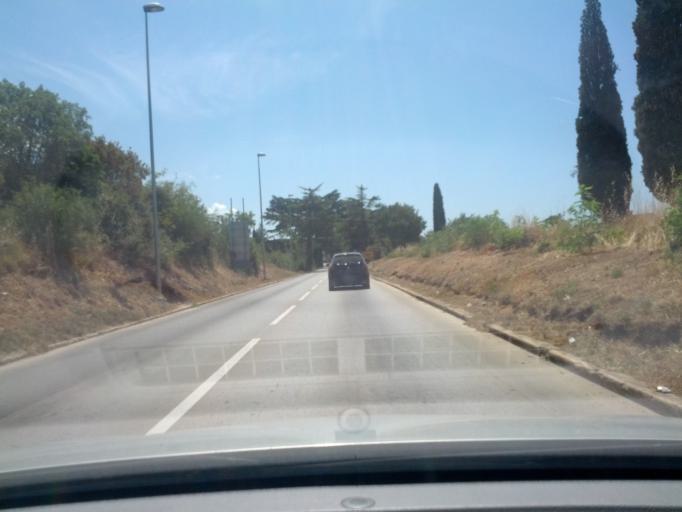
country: HR
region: Istarska
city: Fazana
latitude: 44.9074
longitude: 13.8230
